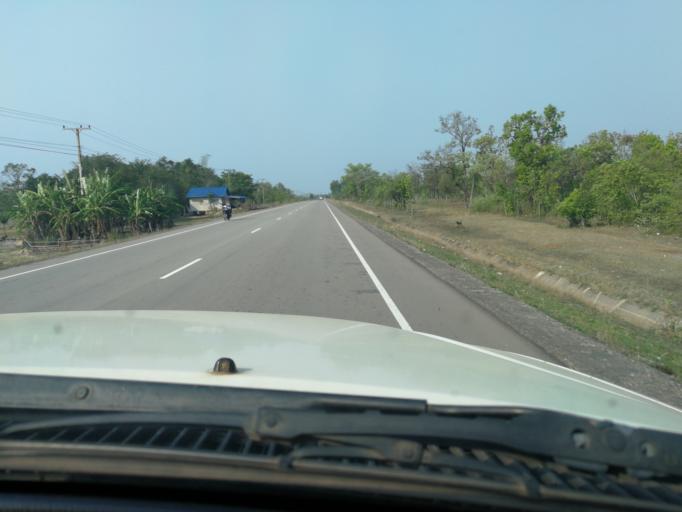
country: TH
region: Mukdahan
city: Wan Yai
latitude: 16.7085
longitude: 105.2394
